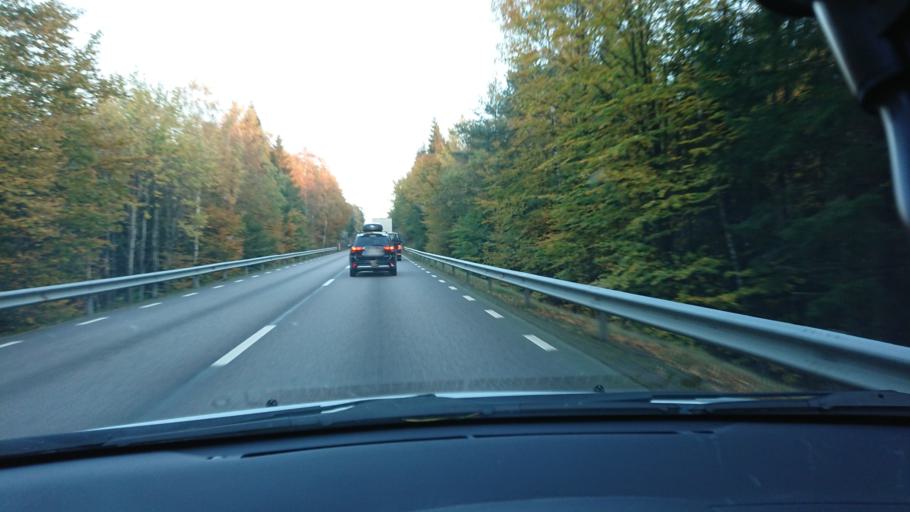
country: SE
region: Halland
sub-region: Laholms Kommun
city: Veinge
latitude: 56.7206
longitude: 13.1712
